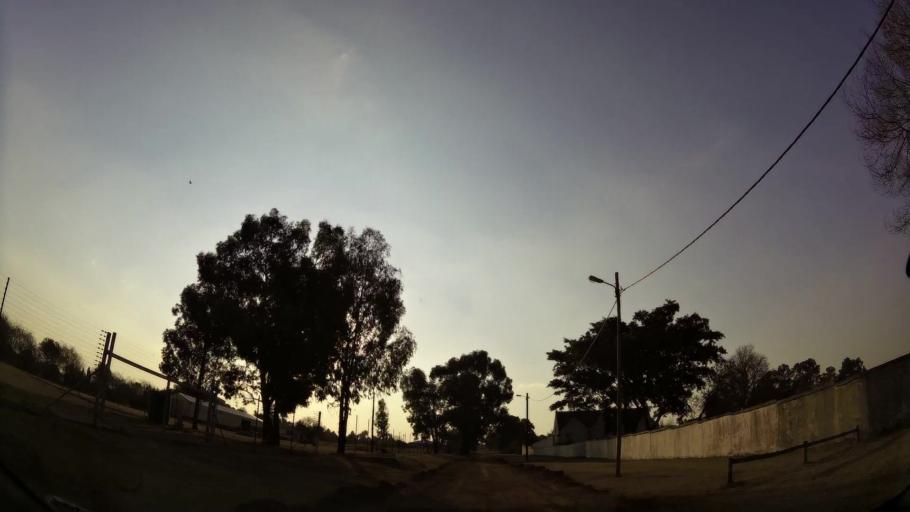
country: ZA
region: Gauteng
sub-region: Ekurhuleni Metropolitan Municipality
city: Benoni
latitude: -26.1558
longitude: 28.3688
